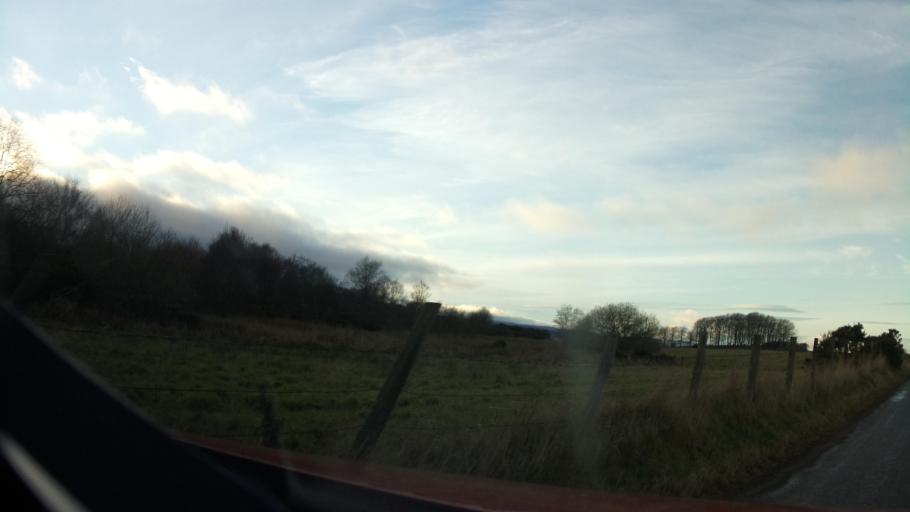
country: GB
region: Scotland
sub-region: Angus
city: Letham
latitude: 56.5779
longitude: -2.7820
